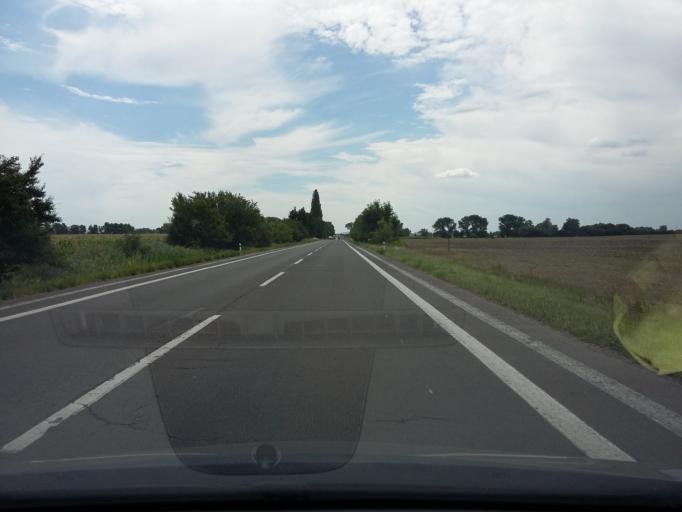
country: SK
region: Bratislavsky
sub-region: Okres Malacky
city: Malacky
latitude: 48.4637
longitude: 17.0109
